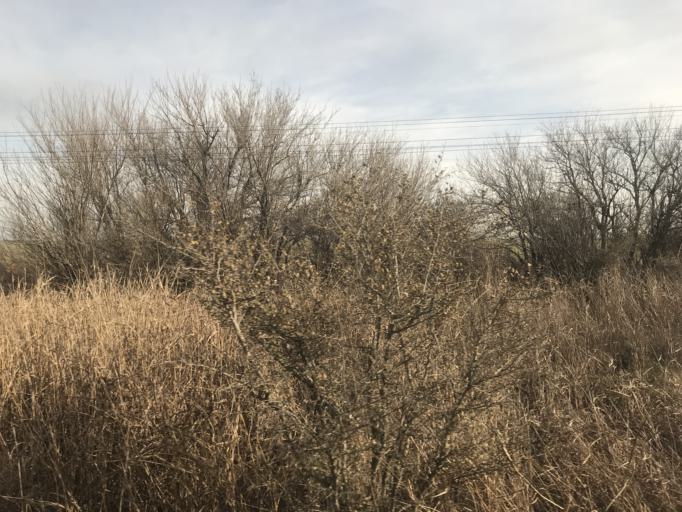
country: AR
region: Cordoba
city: Laguna Larga
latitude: -31.7578
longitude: -63.8197
